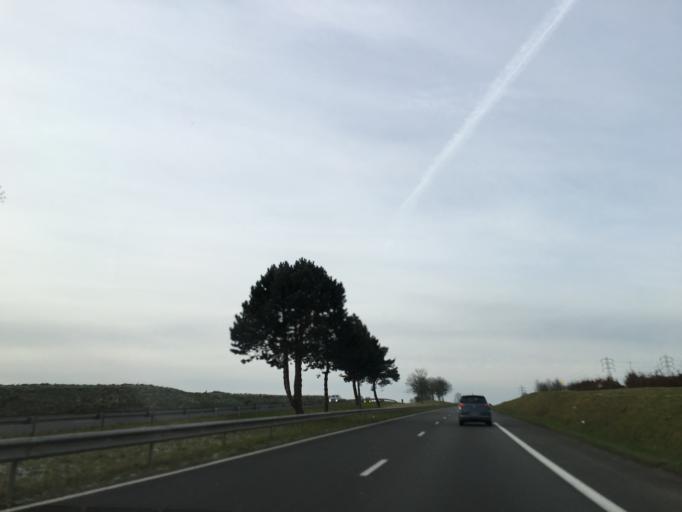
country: FR
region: Nord-Pas-de-Calais
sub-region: Departement du Pas-de-Calais
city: Bailleul-Sir-Berthoult
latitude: 50.3191
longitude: 2.8514
